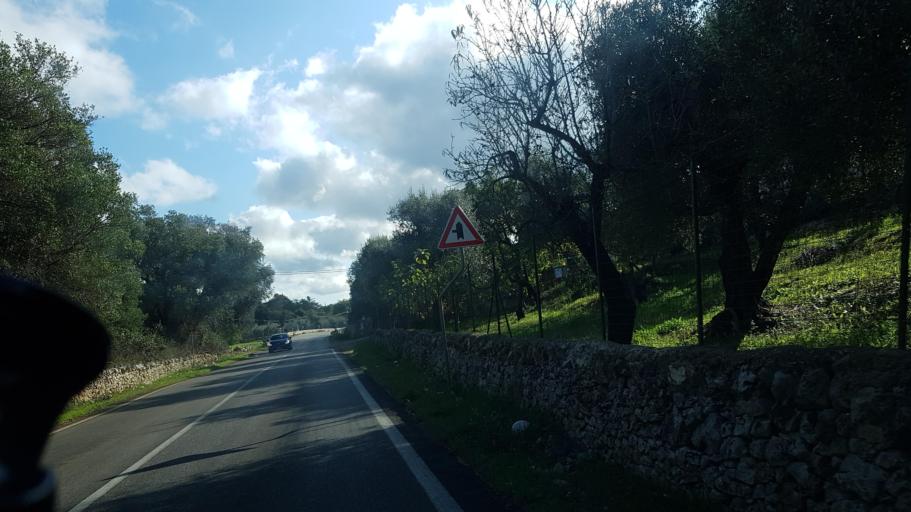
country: IT
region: Apulia
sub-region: Provincia di Brindisi
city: Ostuni
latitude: 40.6928
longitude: 17.5883
